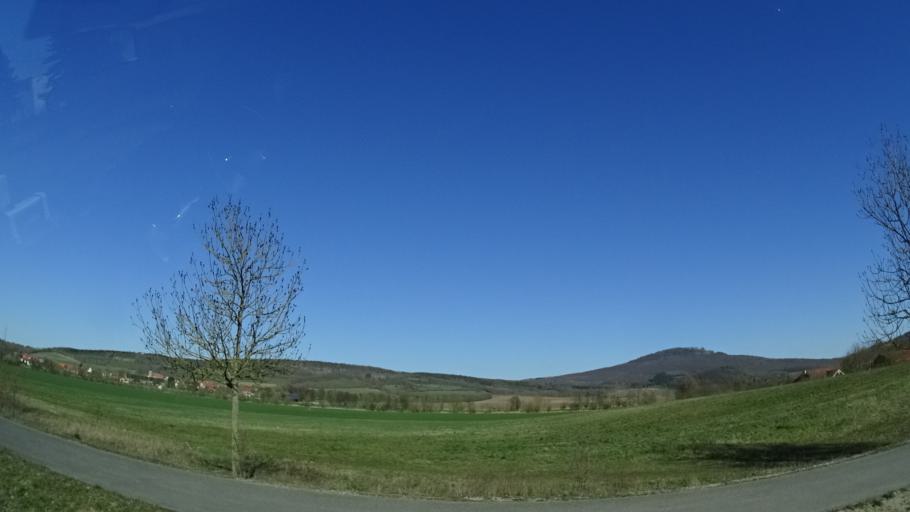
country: DE
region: Thuringia
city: Romhild
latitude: 50.4076
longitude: 10.5367
